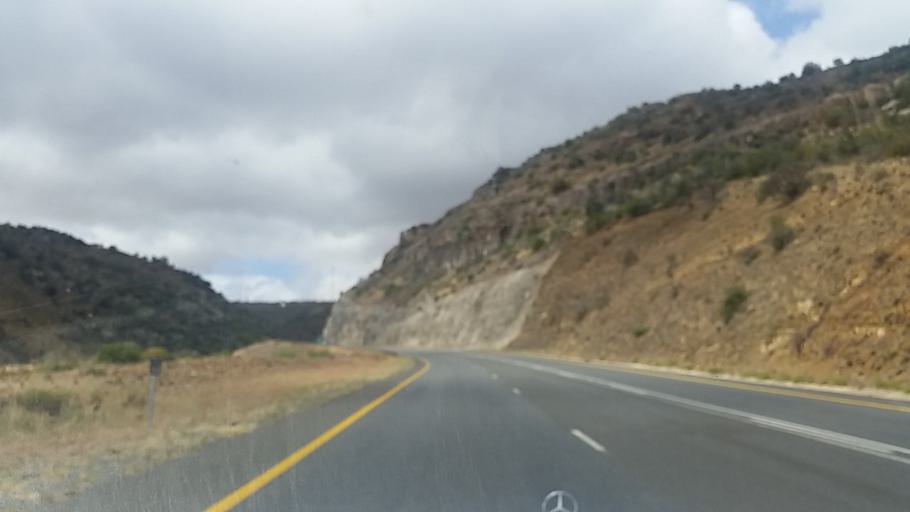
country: ZA
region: Eastern Cape
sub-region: Cacadu District Municipality
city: Graaff-Reinet
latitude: -31.9696
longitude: 24.7159
